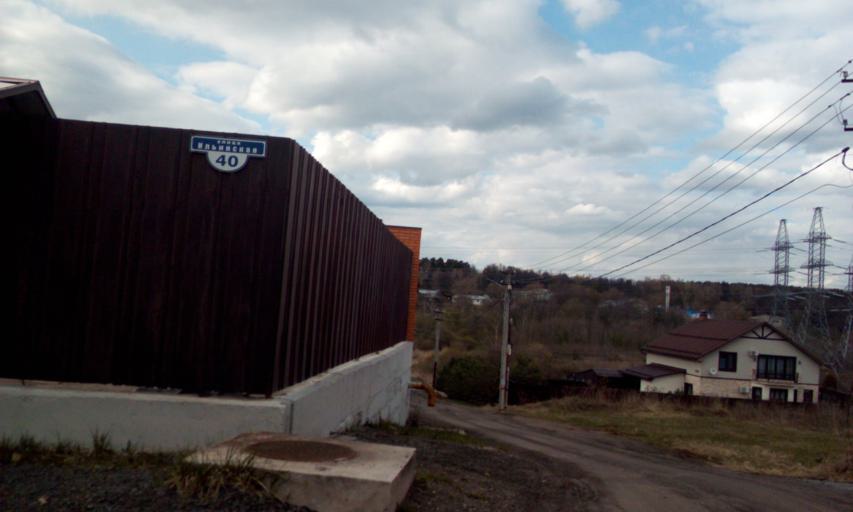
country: RU
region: Moscow
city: Tolstopal'tsevo
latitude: 55.6252
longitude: 37.2569
